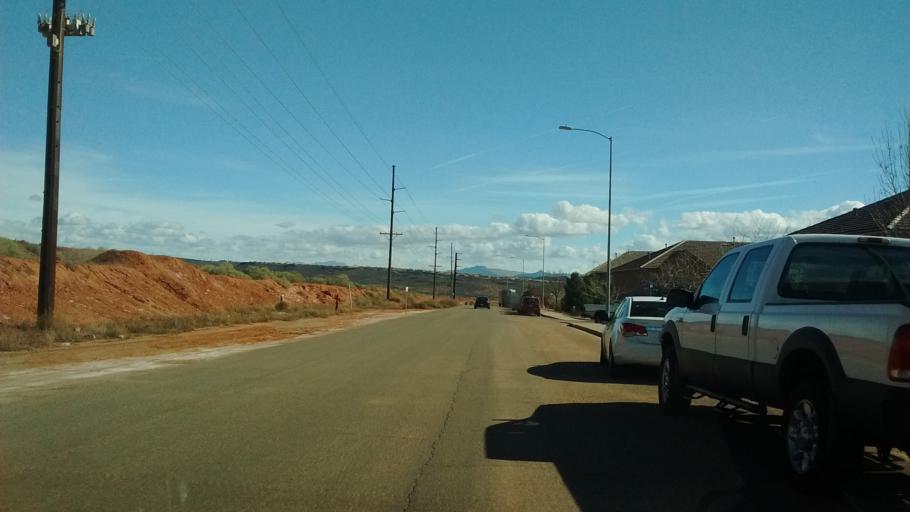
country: US
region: Utah
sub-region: Washington County
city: Washington
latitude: 37.1412
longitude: -113.4950
